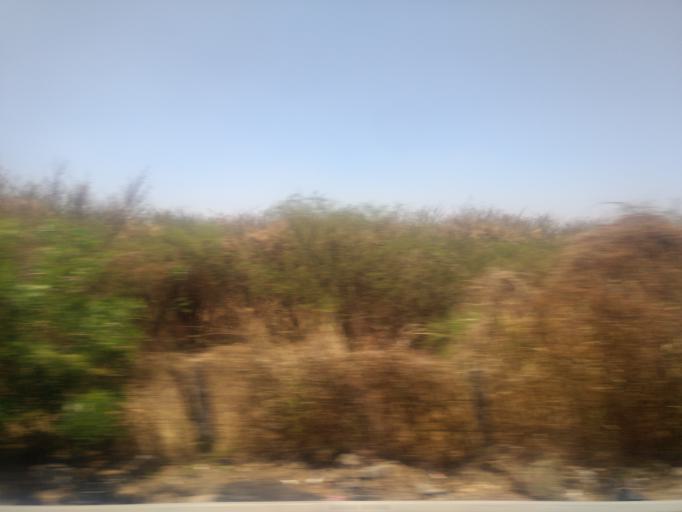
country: MX
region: Colima
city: Cuauhtemoc
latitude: 19.3030
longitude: -103.6264
